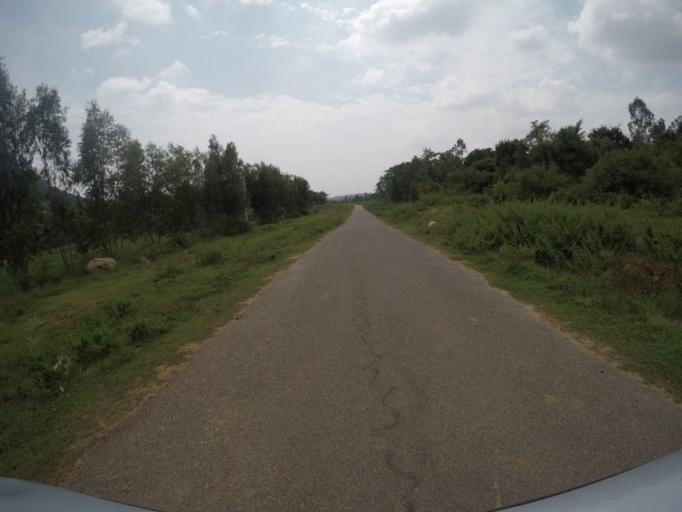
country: IN
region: Karnataka
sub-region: Ramanagara
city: Kanakapura
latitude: 12.4703
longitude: 77.3436
